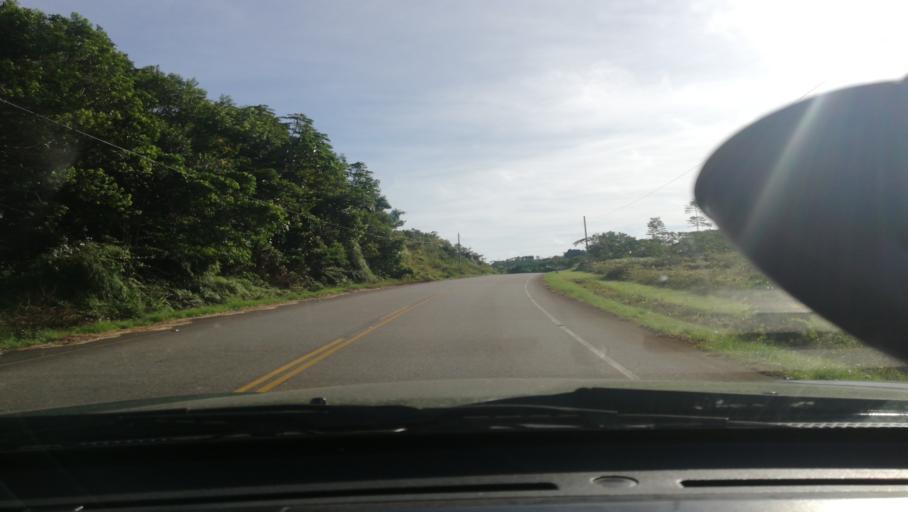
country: PE
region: Loreto
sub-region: Provincia de Loreto
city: Nauta
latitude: -4.4001
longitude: -73.5749
